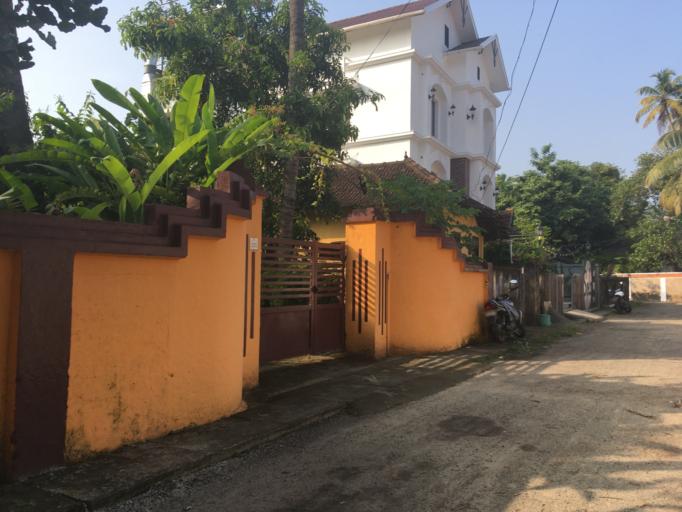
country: IN
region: Kerala
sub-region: Ernakulam
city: Cochin
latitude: 9.9600
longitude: 76.2397
